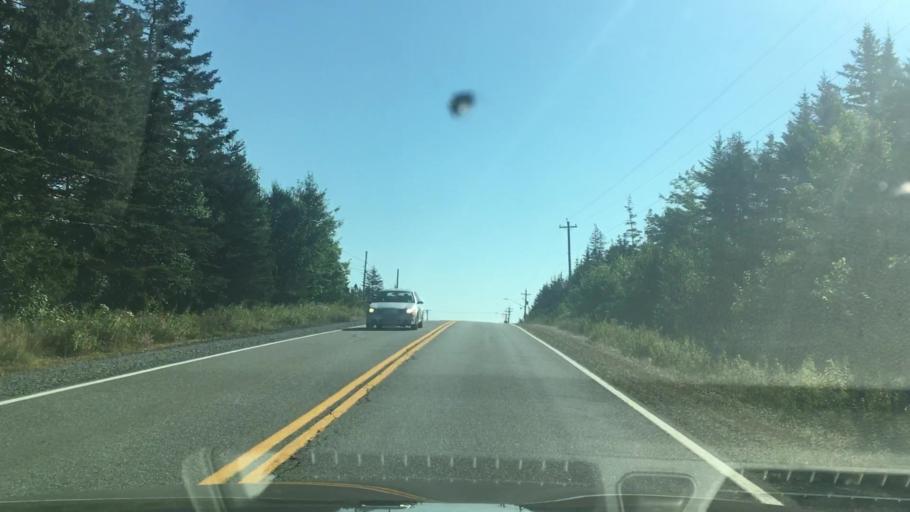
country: CA
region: Nova Scotia
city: Cole Harbour
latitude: 44.7795
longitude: -63.0007
